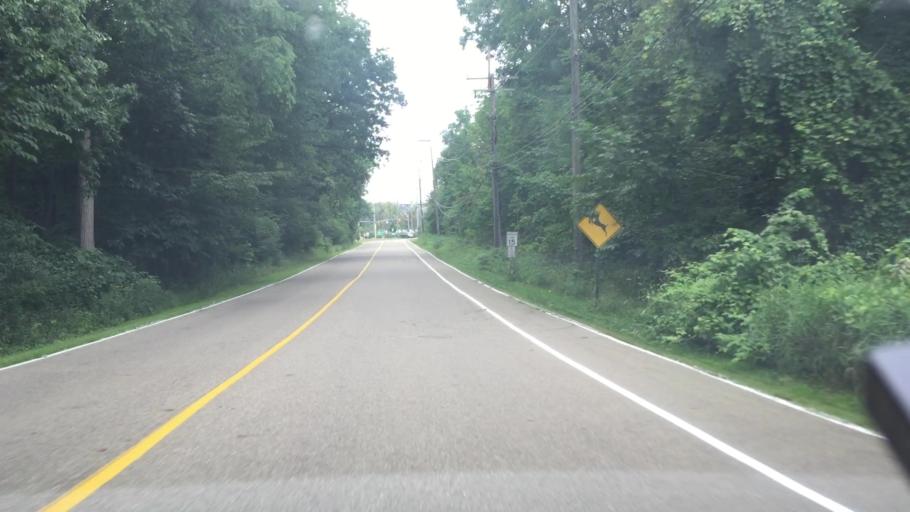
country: US
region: Michigan
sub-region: Oakland County
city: Auburn Hills
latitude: 42.6468
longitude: -83.2288
